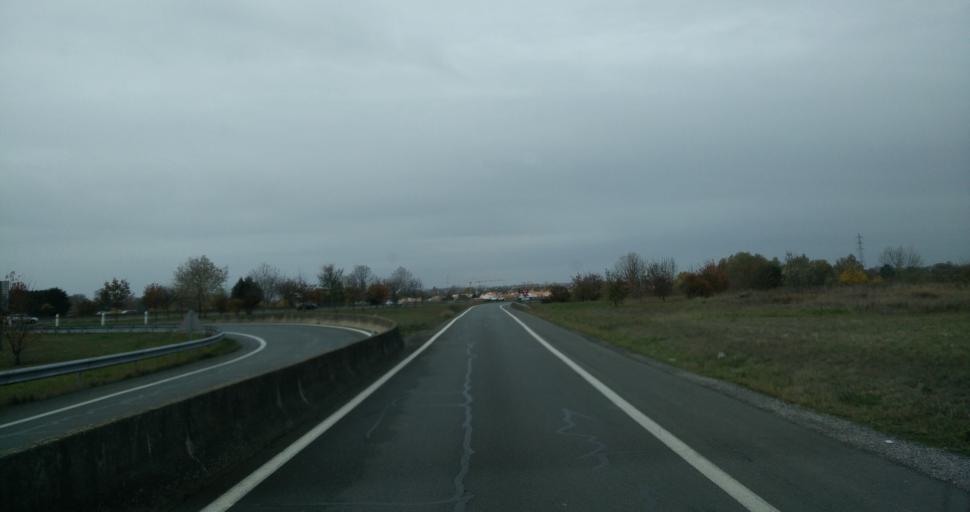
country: FR
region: Poitou-Charentes
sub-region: Departement de la Charente-Maritime
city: Puilboreau
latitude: 46.1777
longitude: -1.1253
